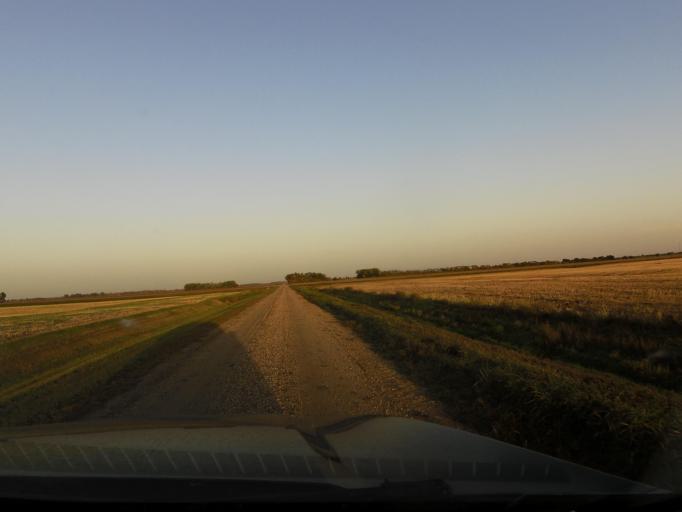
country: US
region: North Dakota
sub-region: Walsh County
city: Grafton
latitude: 48.3832
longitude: -97.2153
